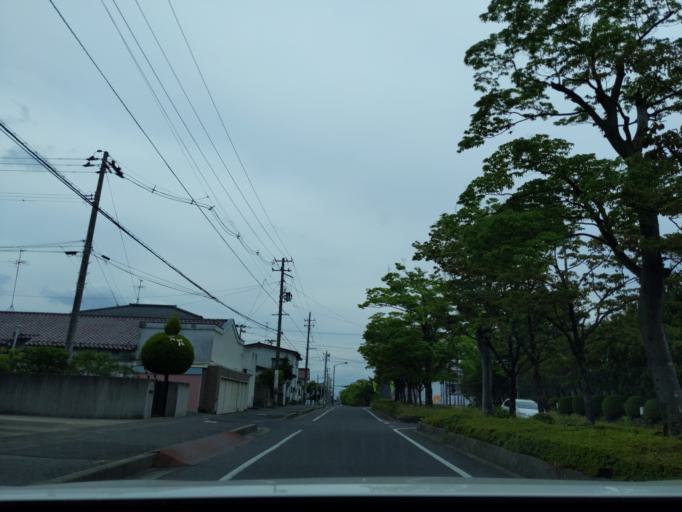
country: JP
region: Fukushima
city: Koriyama
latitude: 37.3915
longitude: 140.3645
